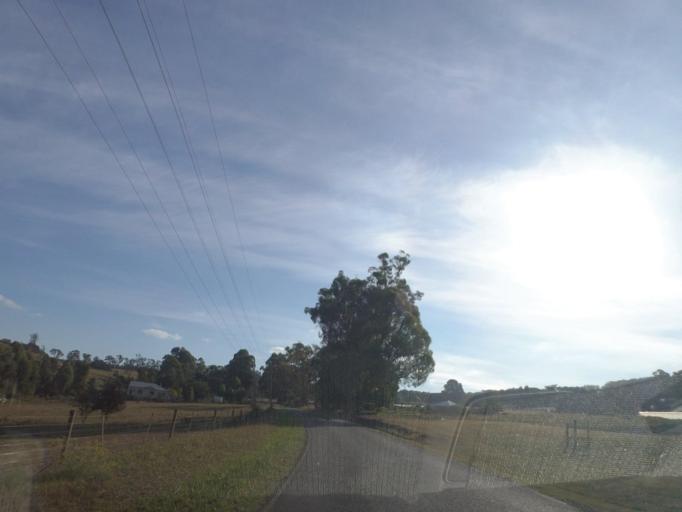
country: AU
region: Victoria
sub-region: Yarra Ranges
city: Monbulk
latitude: -37.8406
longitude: 145.4343
